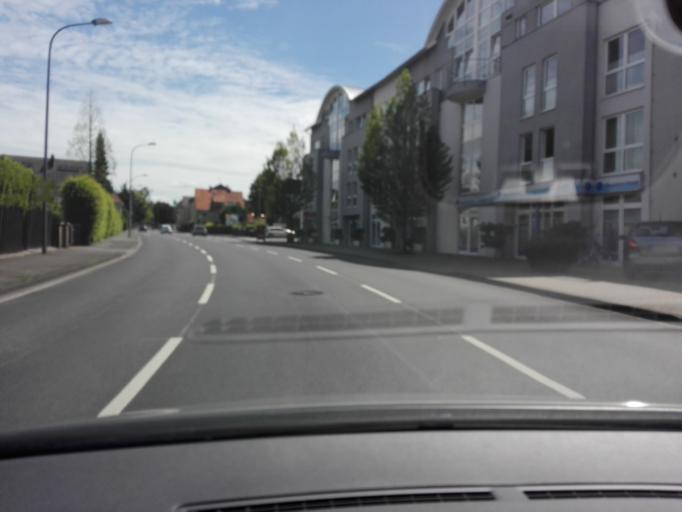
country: DE
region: North Rhine-Westphalia
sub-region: Regierungsbezirk Arnsberg
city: Unna
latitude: 51.5331
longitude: 7.6824
